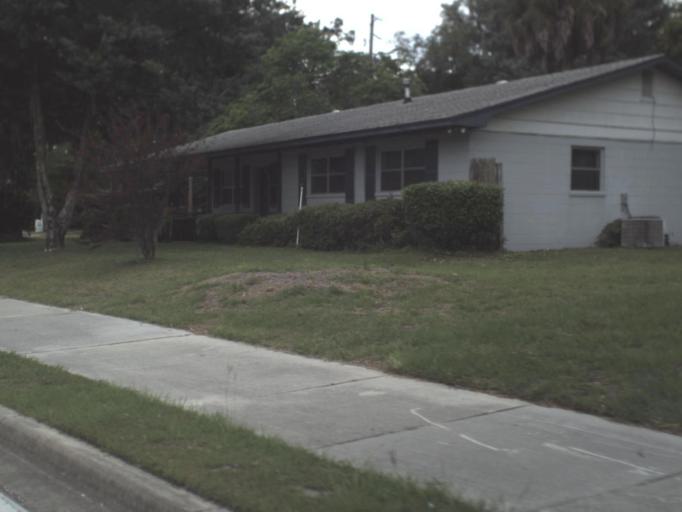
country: US
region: Florida
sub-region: Columbia County
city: Watertown
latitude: 30.1823
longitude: -82.6186
